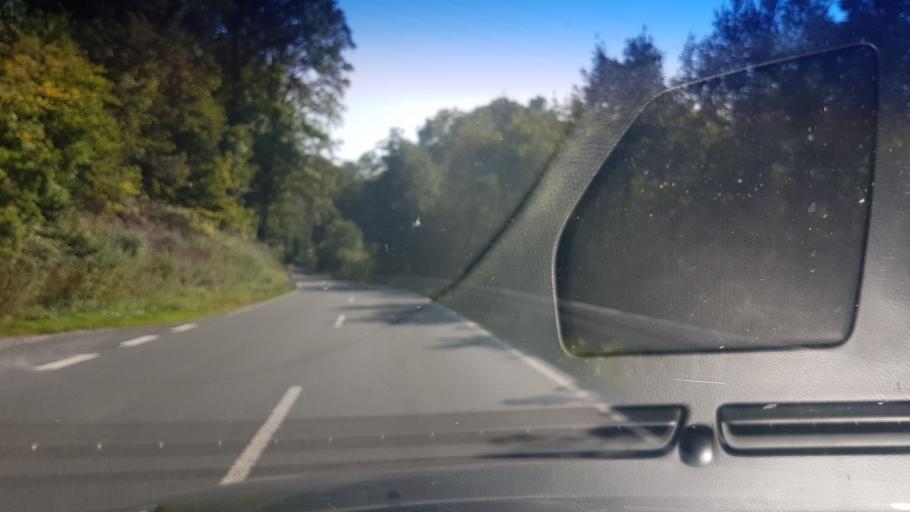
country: DE
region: Bavaria
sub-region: Upper Franconia
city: Bad Berneck im Fichtelgebirge
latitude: 50.0608
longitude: 11.6733
